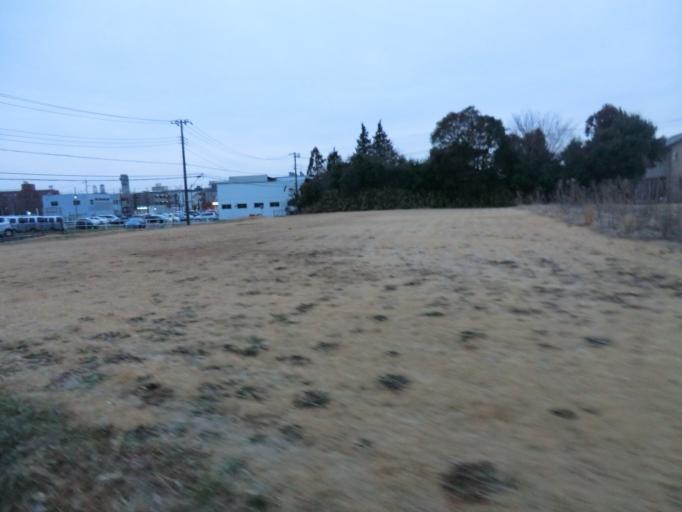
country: JP
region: Ibaraki
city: Naka
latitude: 36.0955
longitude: 140.1129
